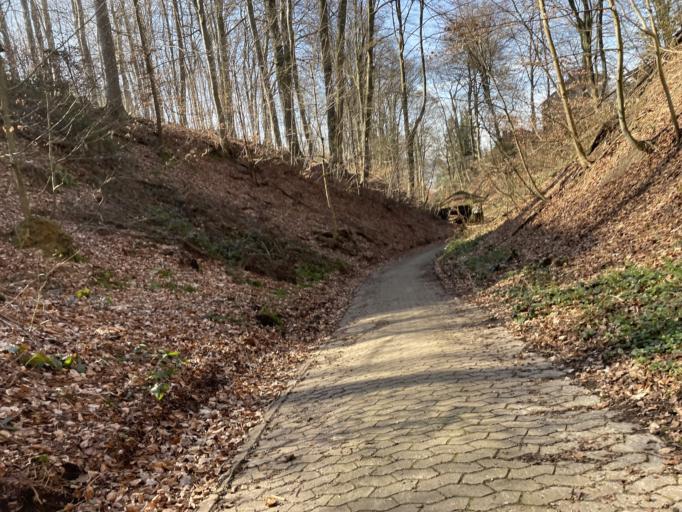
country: DE
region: North Rhine-Westphalia
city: Porta Westfalica
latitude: 52.2349
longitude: 8.9302
